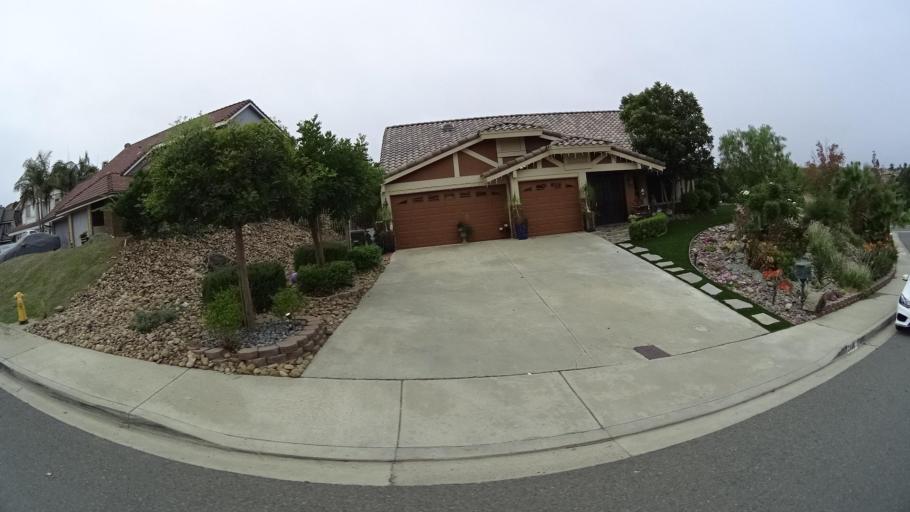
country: US
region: California
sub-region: San Diego County
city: Rancho San Diego
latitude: 32.7571
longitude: -116.9098
